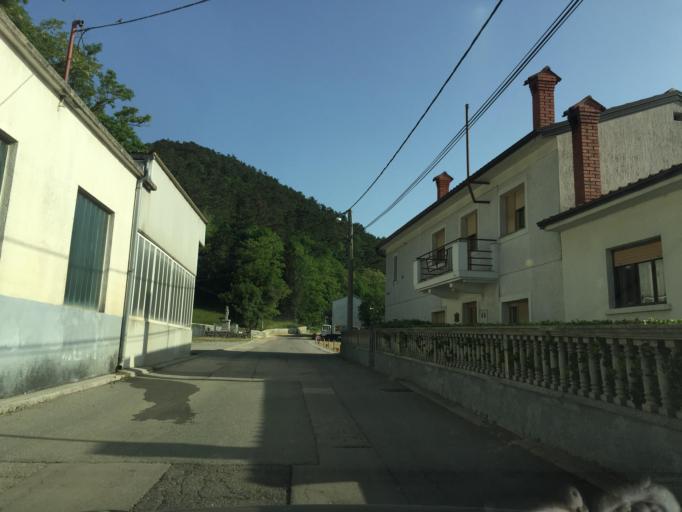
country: HR
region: Primorsko-Goranska
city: Klana
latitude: 45.4518
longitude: 14.3777
